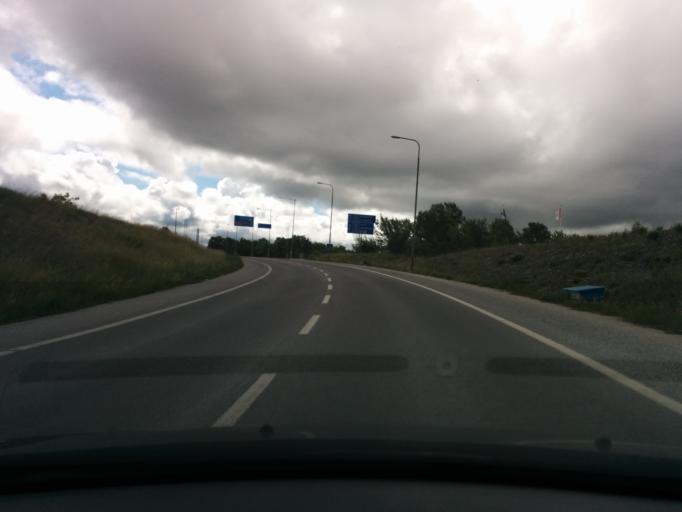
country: SE
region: Gotland
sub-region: Gotland
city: Visby
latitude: 57.6239
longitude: 18.2732
